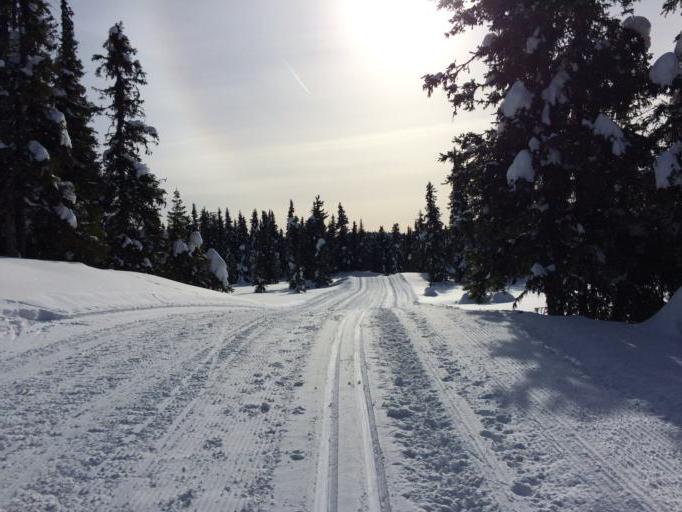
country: NO
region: Oppland
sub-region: Gausdal
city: Segalstad bru
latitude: 61.3302
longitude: 10.0827
